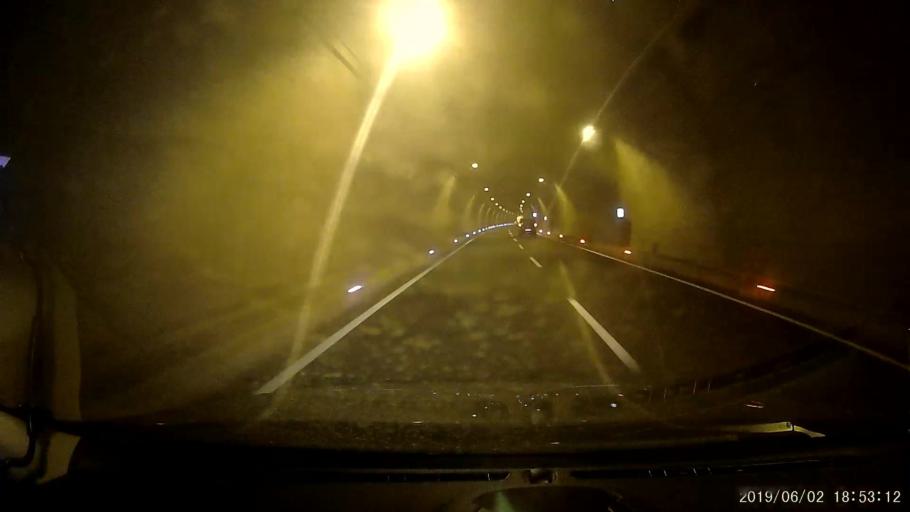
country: TR
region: Ordu
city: Ordu
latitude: 40.9818
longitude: 37.8274
